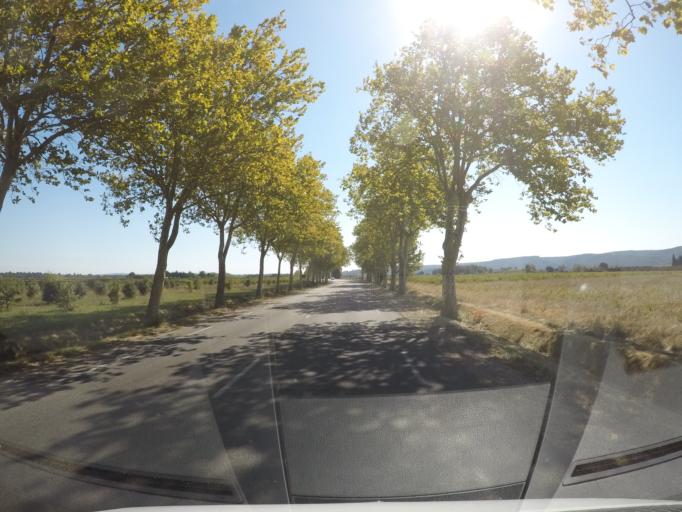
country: FR
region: Languedoc-Roussillon
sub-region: Departement du Gard
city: Castillon-du-Gard
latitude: 43.9703
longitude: 4.5007
